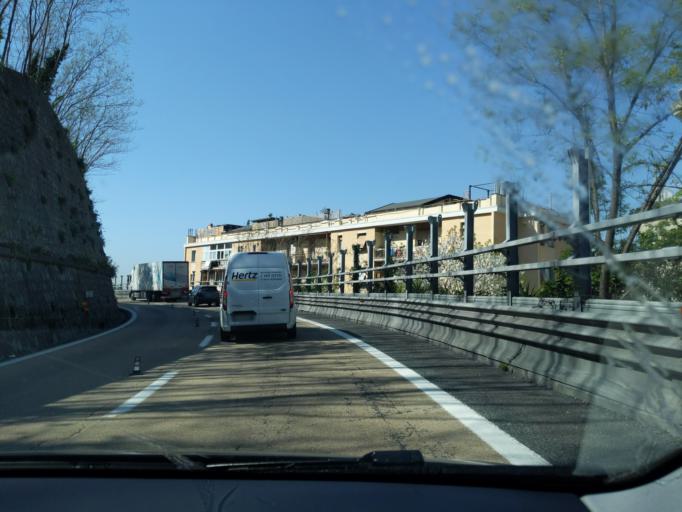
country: IT
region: Liguria
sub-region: Provincia di Genova
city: San Teodoro
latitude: 44.4269
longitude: 8.8960
